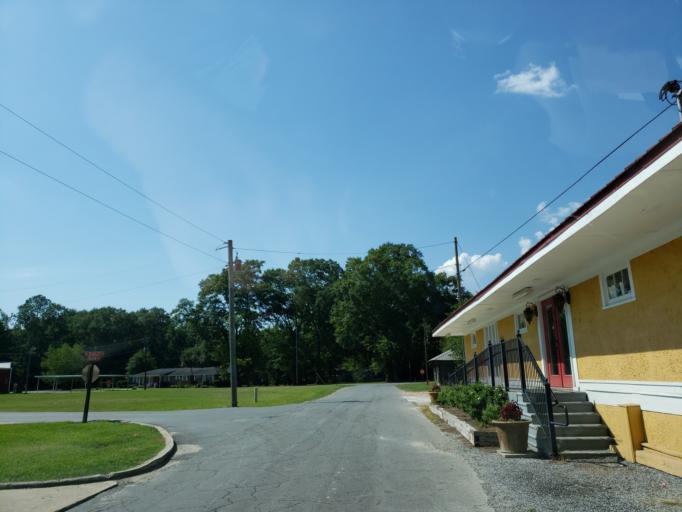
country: US
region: Mississippi
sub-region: Covington County
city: Collins
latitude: 31.5622
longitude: -89.4973
